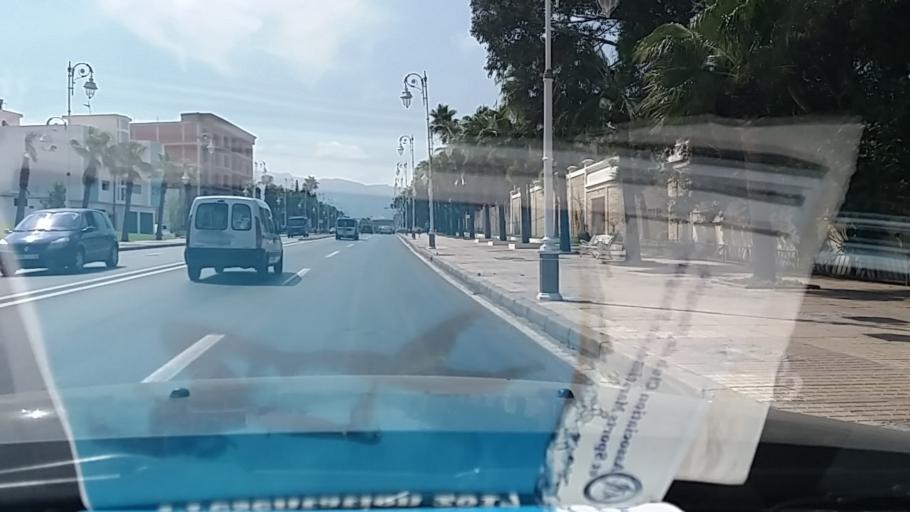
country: MA
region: Tanger-Tetouan
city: Tetouan
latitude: 35.5952
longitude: -5.3408
